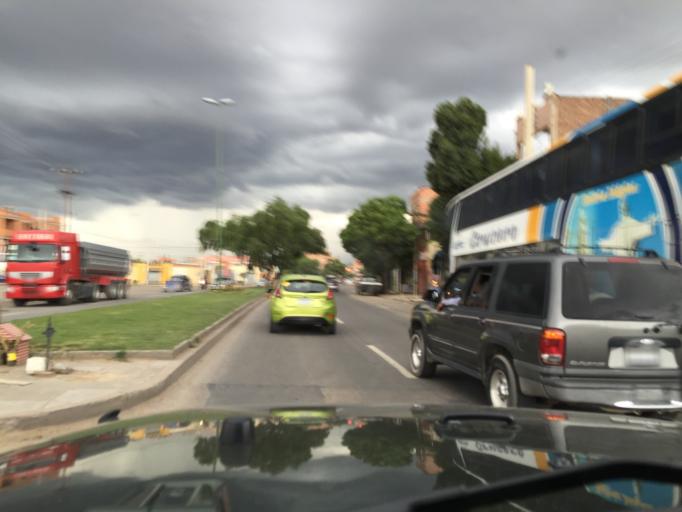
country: BO
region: Cochabamba
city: Cochabamba
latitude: -17.4050
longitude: -66.1792
